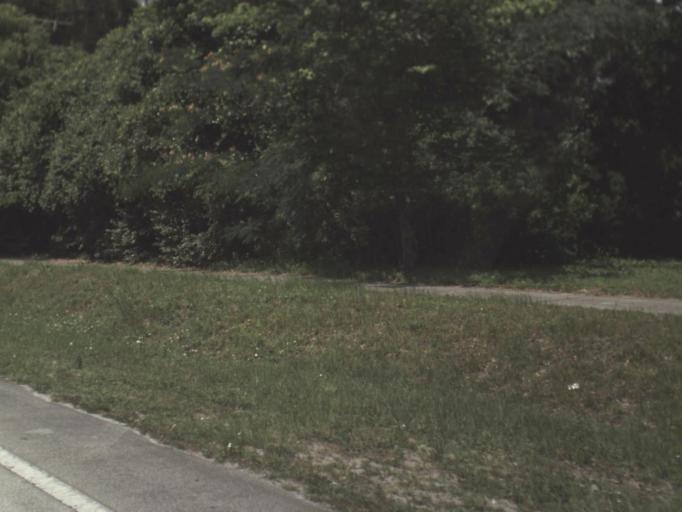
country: US
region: Florida
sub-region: Bradford County
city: Starke
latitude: 29.9580
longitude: -82.0163
